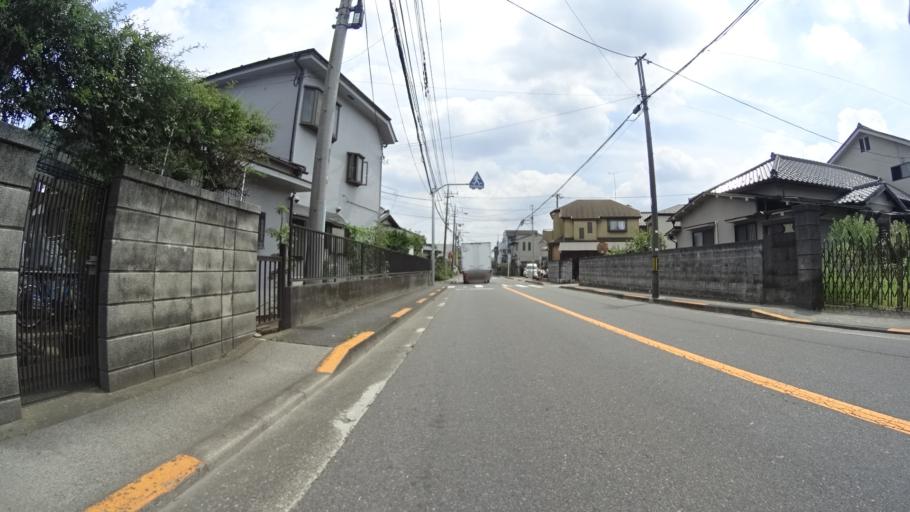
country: JP
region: Tokyo
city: Fussa
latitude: 35.7598
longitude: 139.3062
